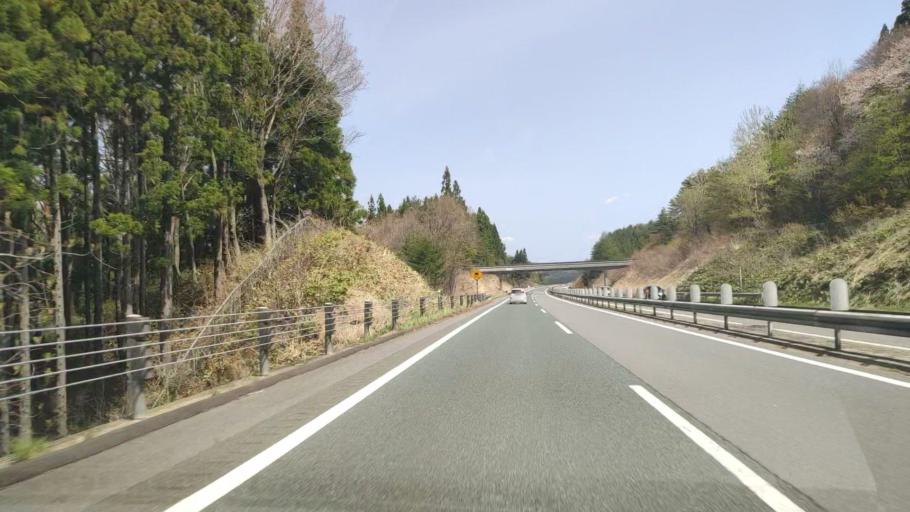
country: JP
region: Iwate
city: Ichinohe
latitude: 40.1508
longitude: 141.1181
